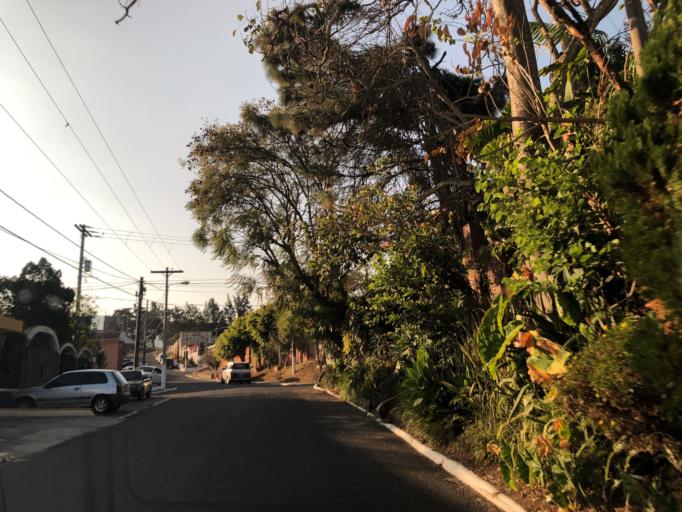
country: GT
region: Guatemala
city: Mixco
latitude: 14.6268
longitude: -90.5951
